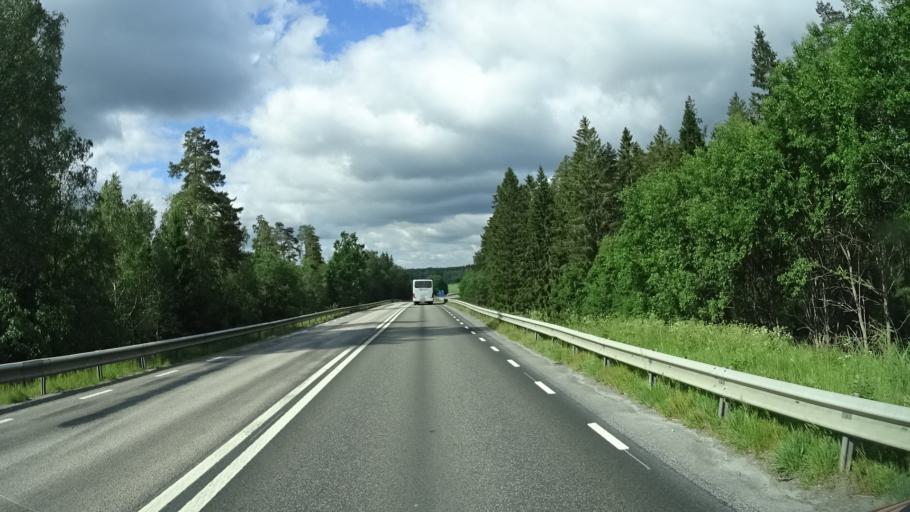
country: SE
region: Kronoberg
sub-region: Alvesta Kommun
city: Alvesta
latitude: 56.9105
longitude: 14.4778
